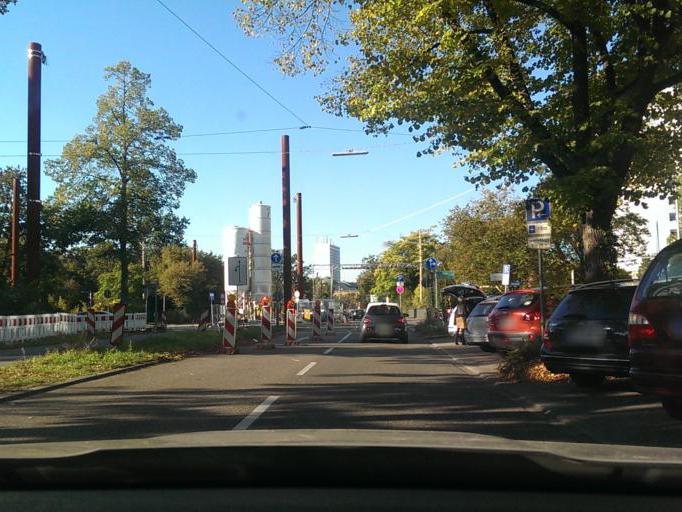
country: DE
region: Baden-Wuerttemberg
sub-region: Karlsruhe Region
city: Karlsruhe
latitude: 48.9988
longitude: 8.4037
